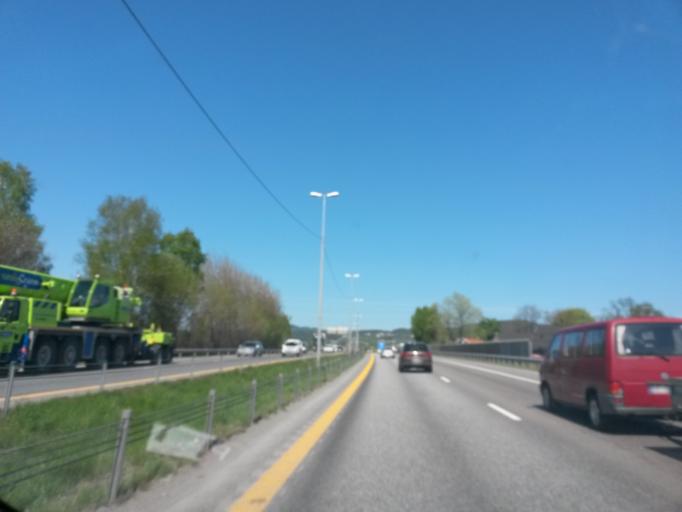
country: NO
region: Buskerud
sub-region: Lier
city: Lierbyen
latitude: 59.7529
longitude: 10.2466
